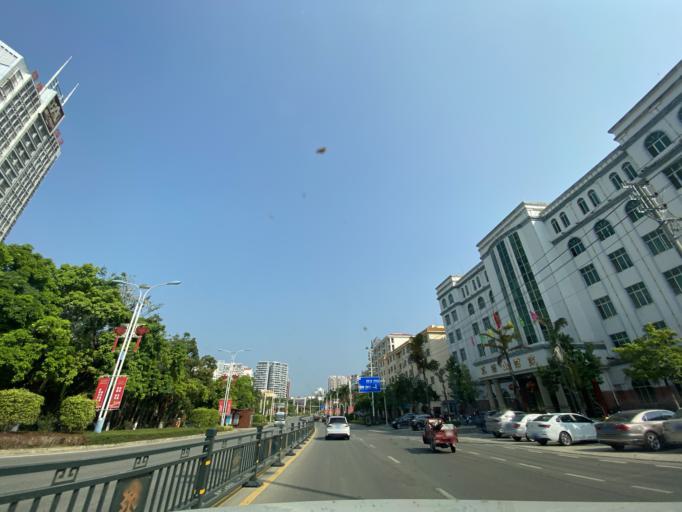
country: CN
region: Hainan
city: Chongshan
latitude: 18.7663
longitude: 109.5201
